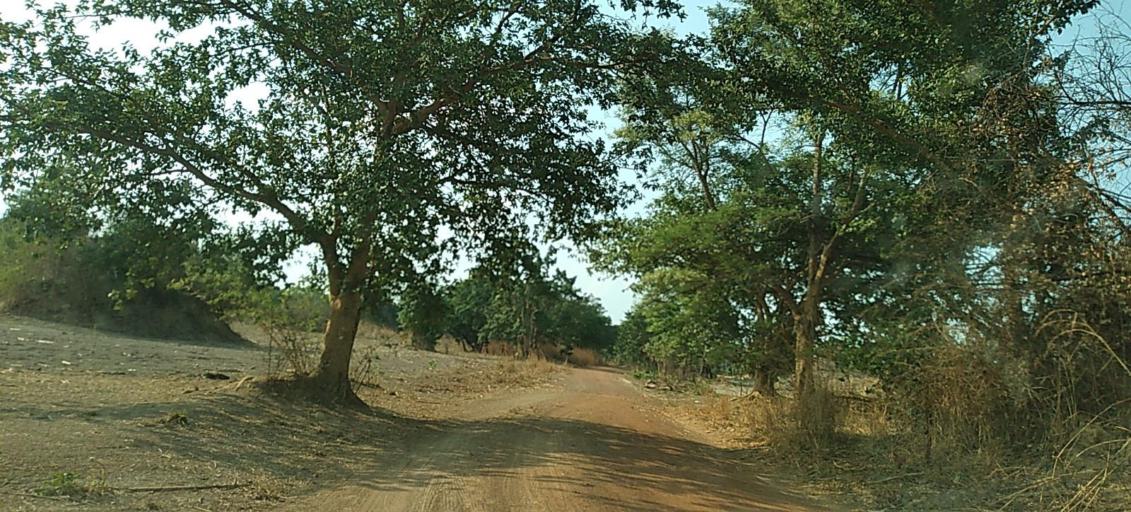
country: ZM
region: Copperbelt
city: Mpongwe
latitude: -13.4539
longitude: 28.0665
